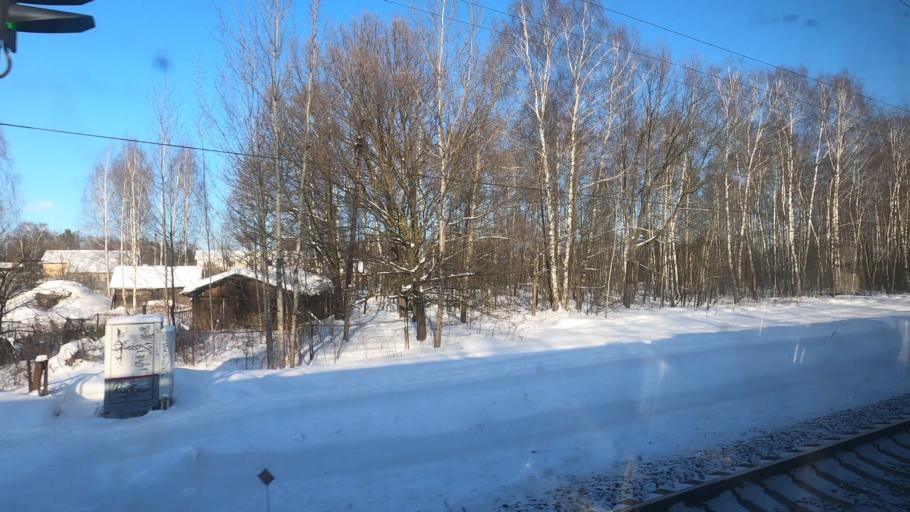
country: RU
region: Moskovskaya
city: Imeni Vorovskogo
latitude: 55.7221
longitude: 38.2983
